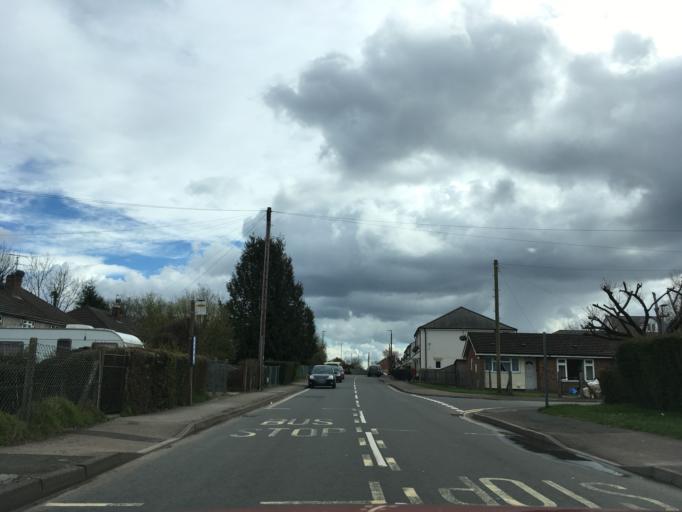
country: GB
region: England
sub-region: Gloucestershire
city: Coleford
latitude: 51.7839
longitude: -2.6098
